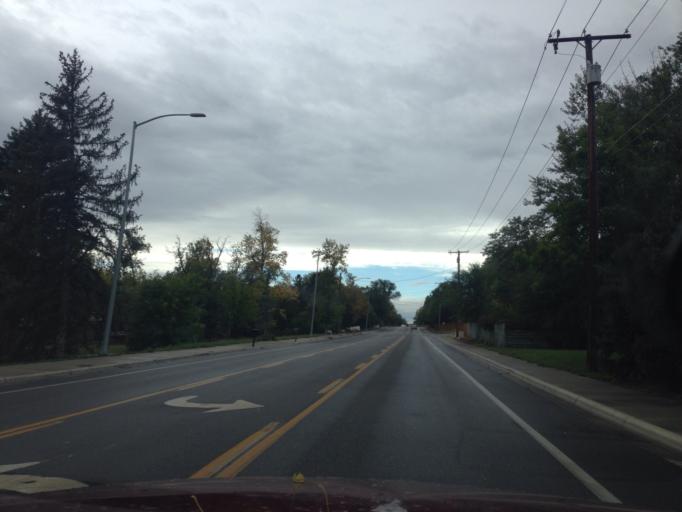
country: US
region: Montana
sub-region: Yellowstone County
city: Billings
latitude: 45.8007
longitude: -108.5663
